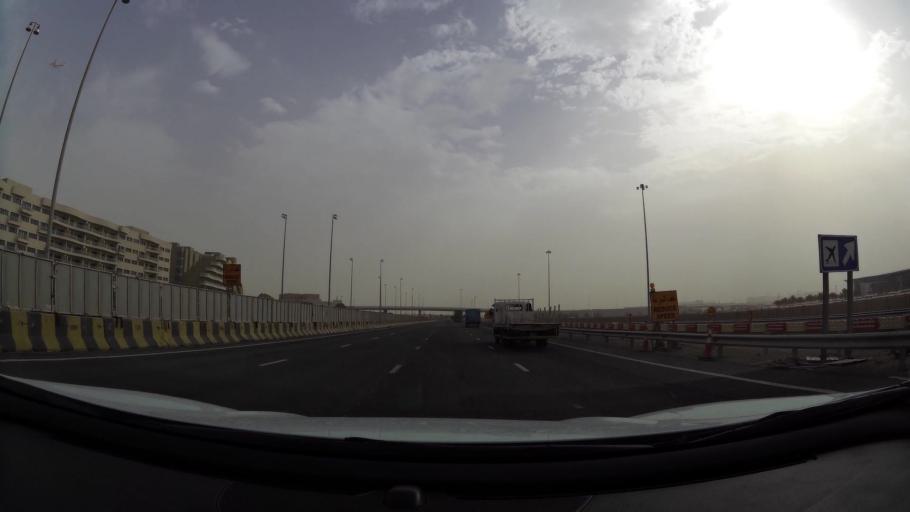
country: AE
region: Abu Dhabi
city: Abu Dhabi
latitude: 24.4483
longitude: 54.6123
